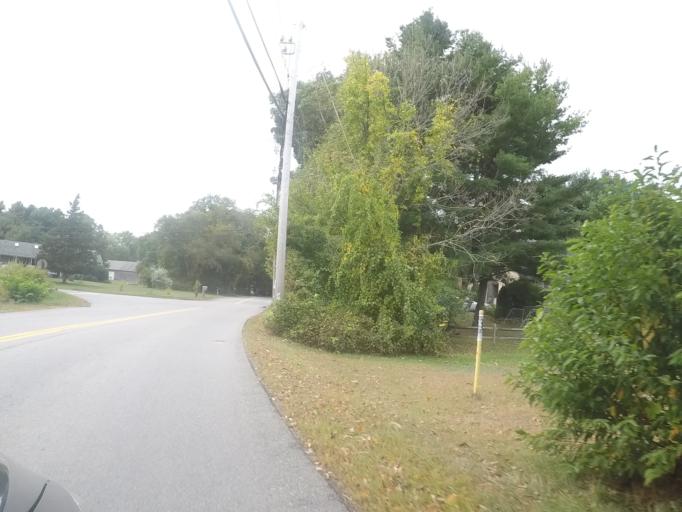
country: US
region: Massachusetts
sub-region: Bristol County
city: Smith Mills
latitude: 41.6786
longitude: -71.0304
